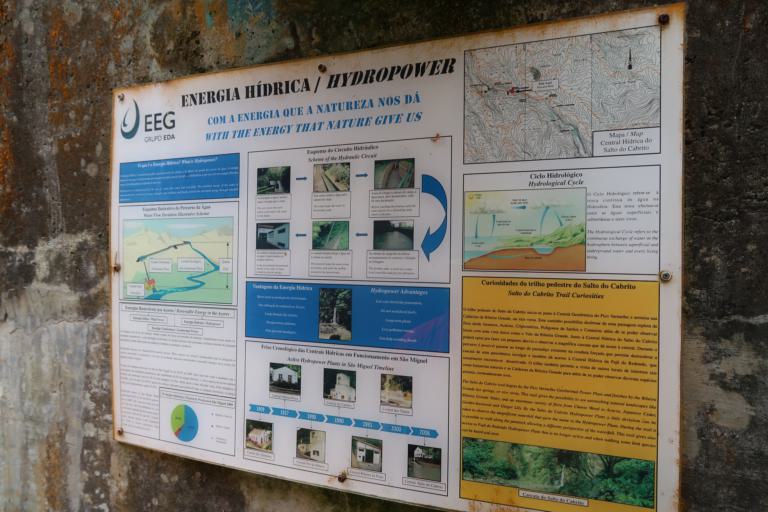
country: PT
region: Azores
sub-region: Ribeira Grande
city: Rabo de Peixe
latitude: 37.7953
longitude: -25.4921
